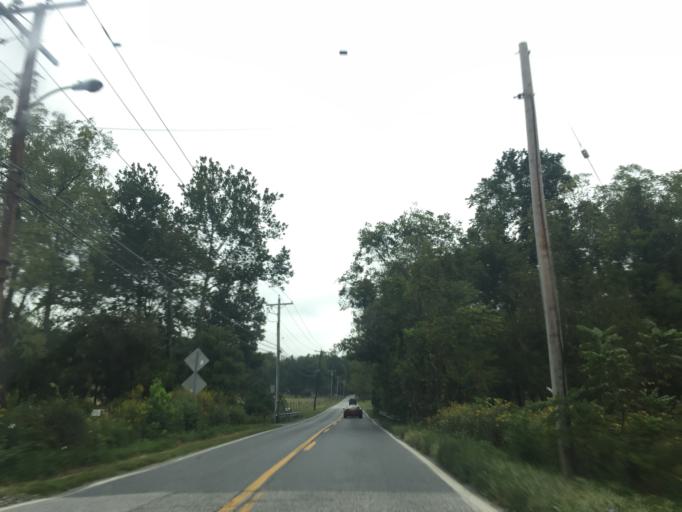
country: US
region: Maryland
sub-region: Baltimore County
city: Carney
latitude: 39.4358
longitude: -76.5238
